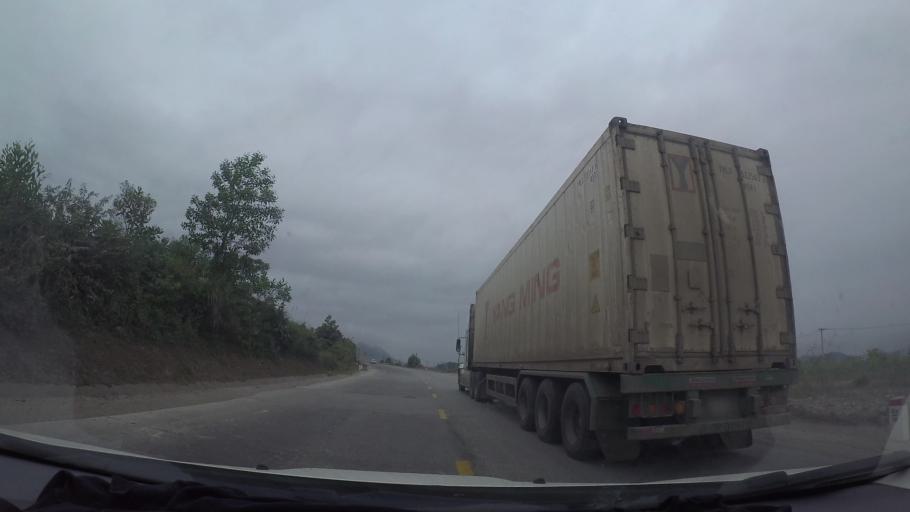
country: VN
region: Da Nang
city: Lien Chieu
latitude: 16.0880
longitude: 108.0848
